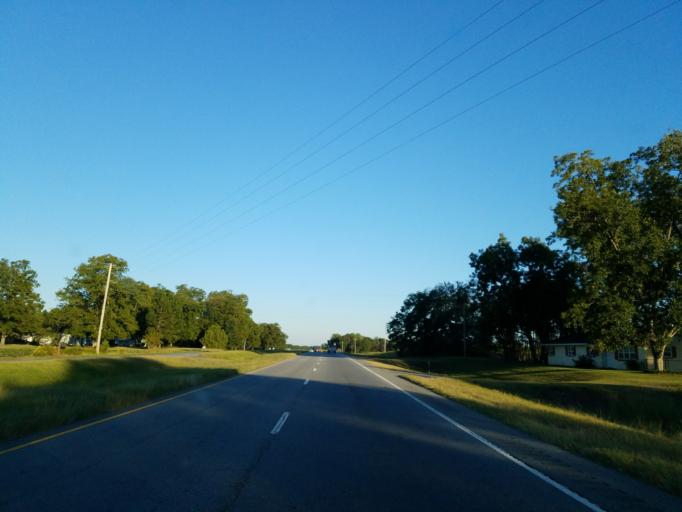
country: US
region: Georgia
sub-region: Worth County
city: Sylvester
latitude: 31.4809
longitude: -83.6881
